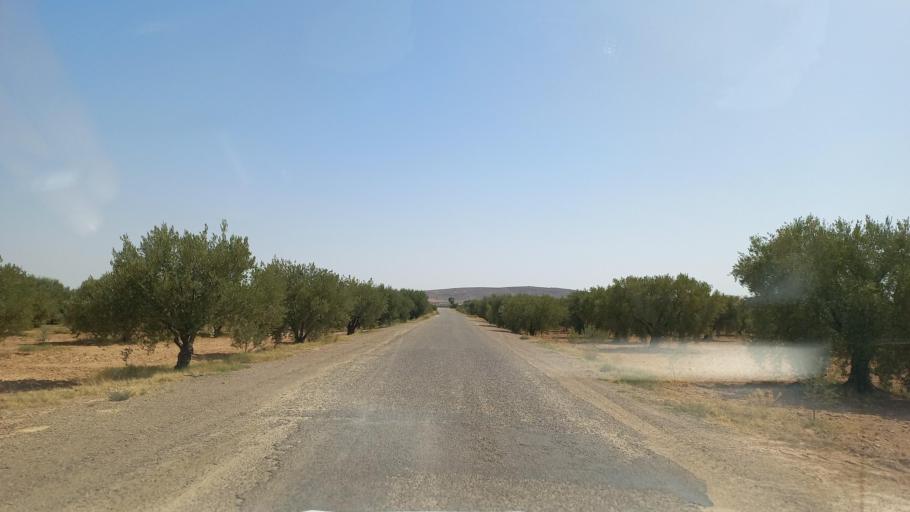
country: TN
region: Al Qasrayn
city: Kasserine
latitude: 35.2165
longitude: 9.0416
